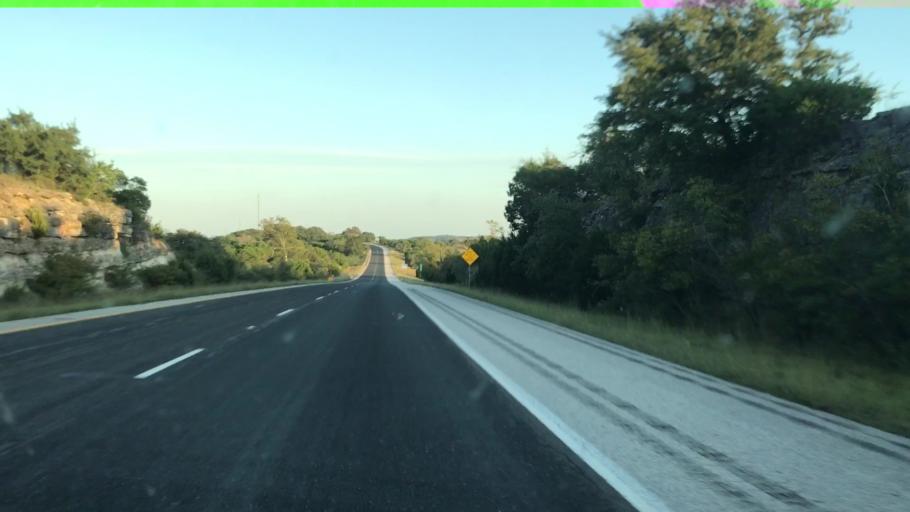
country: US
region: Texas
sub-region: Kerr County
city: Kerrville
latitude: 30.0565
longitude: -99.0407
